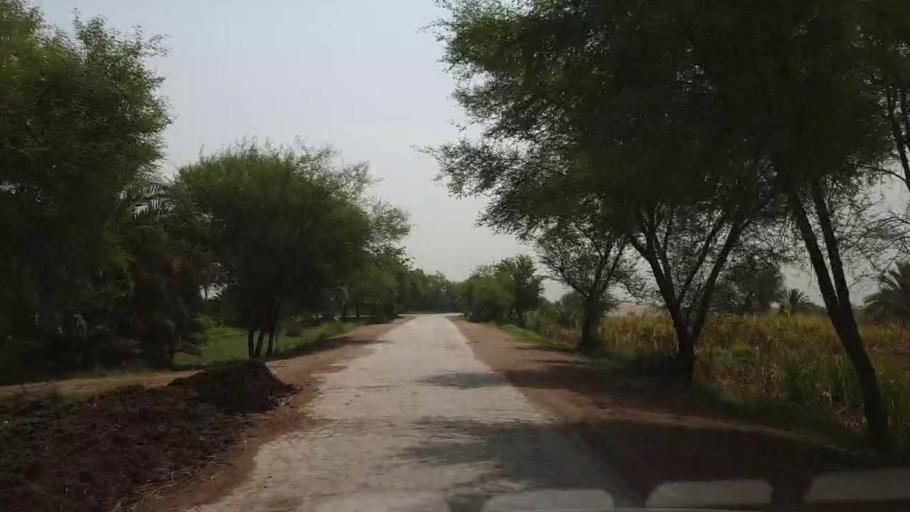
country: PK
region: Sindh
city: Gambat
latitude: 27.4421
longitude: 68.5167
